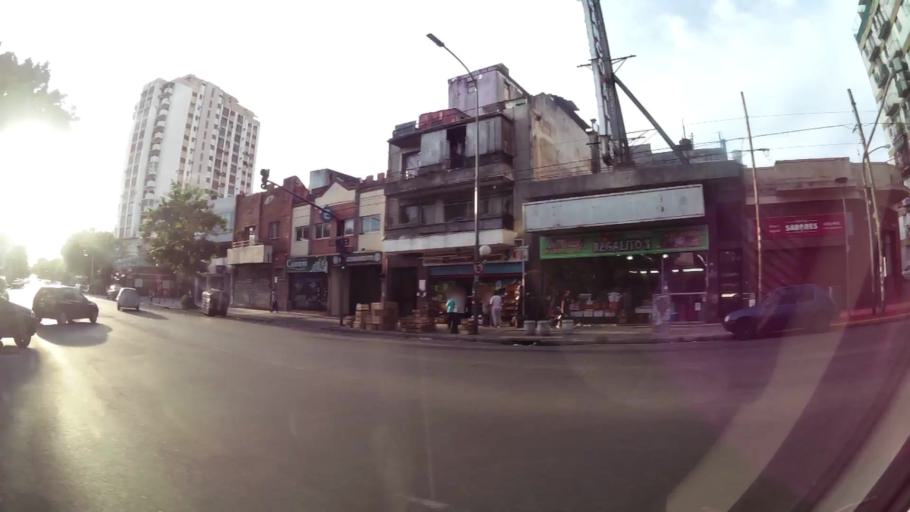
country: AR
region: Buenos Aires F.D.
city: Villa Santa Rita
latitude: -34.6345
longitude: -58.4351
